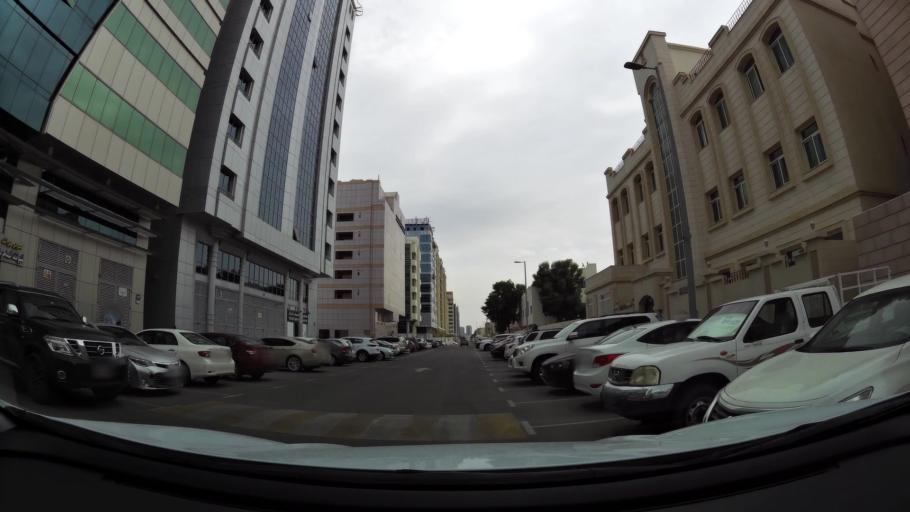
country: AE
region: Abu Dhabi
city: Abu Dhabi
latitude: 24.4399
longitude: 54.4083
